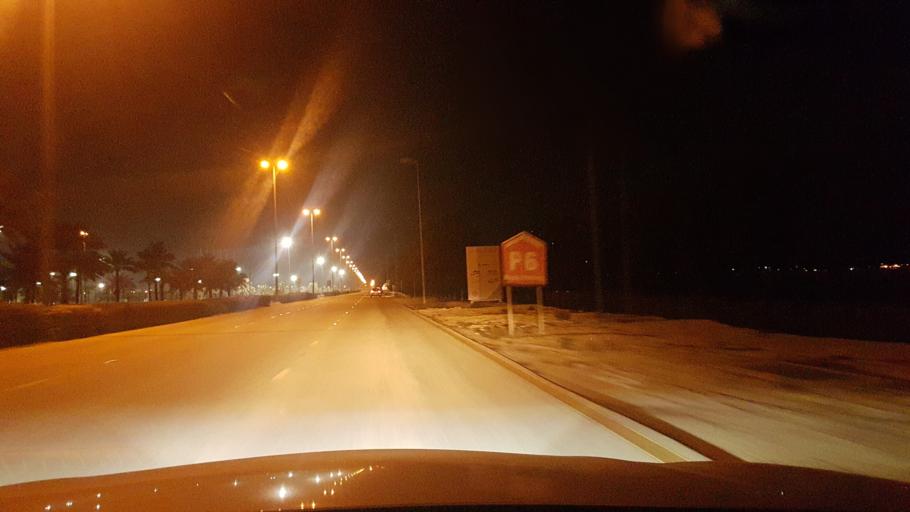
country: BH
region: Central Governorate
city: Dar Kulayb
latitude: 26.0363
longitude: 50.5050
